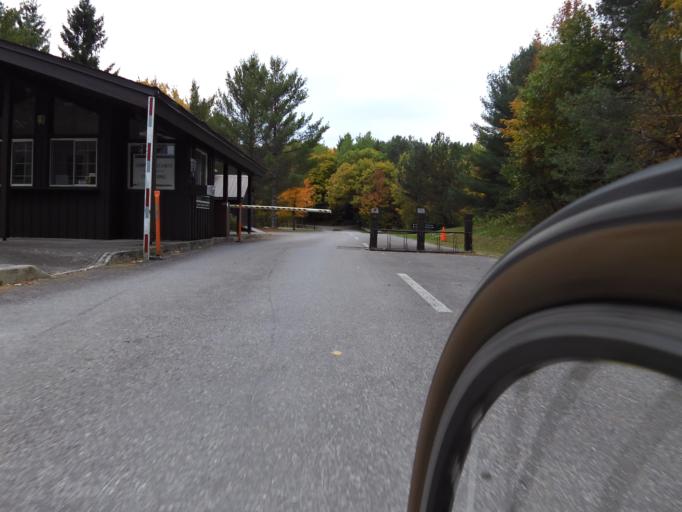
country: CA
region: Quebec
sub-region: Outaouais
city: Wakefield
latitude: 45.6056
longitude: -76.0130
